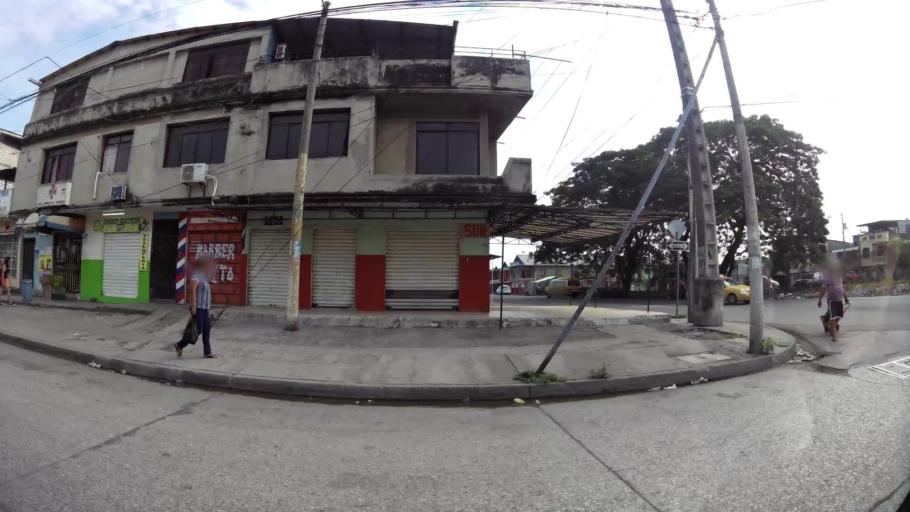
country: EC
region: Guayas
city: Guayaquil
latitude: -2.2437
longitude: -79.8867
